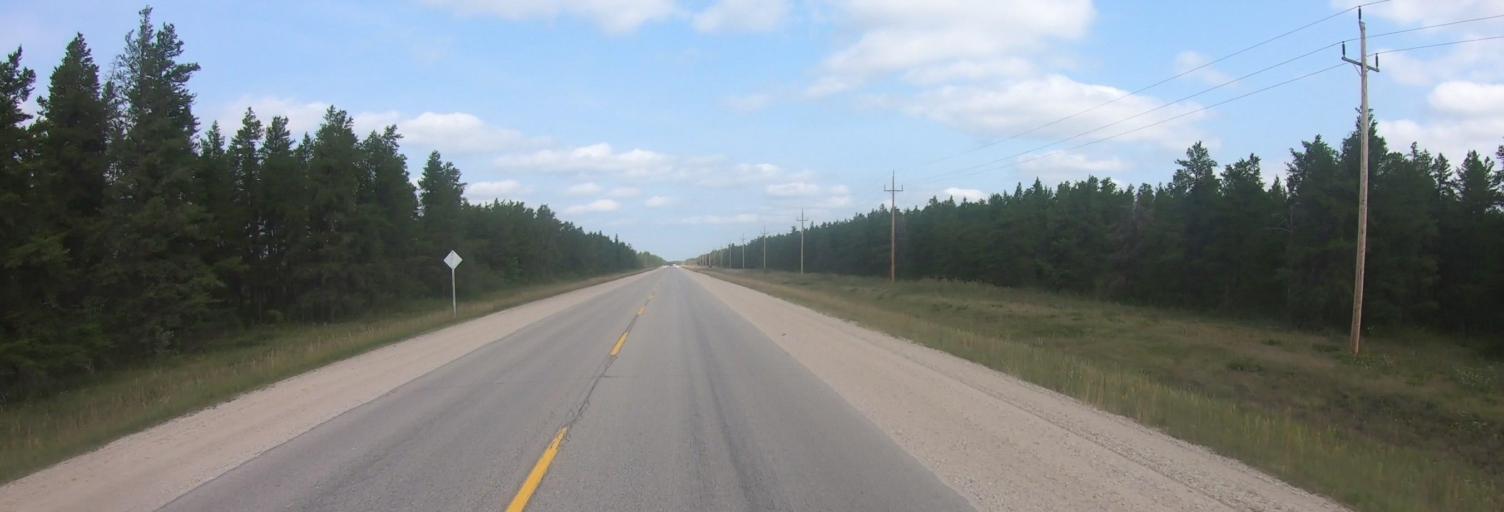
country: CA
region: Manitoba
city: La Broquerie
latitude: 49.2415
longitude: -96.3470
